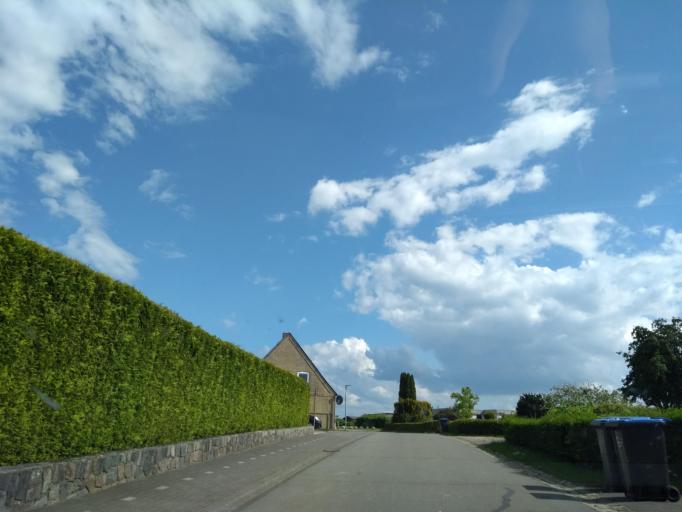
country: DE
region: Schleswig-Holstein
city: Thumby
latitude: 54.5575
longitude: 9.9229
